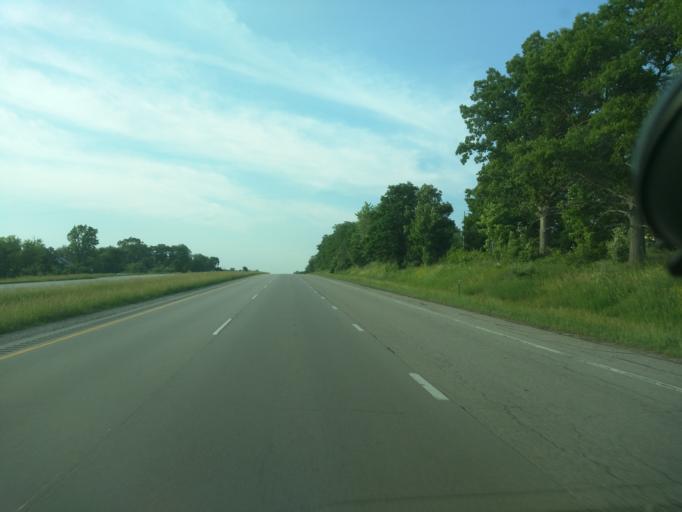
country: US
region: Michigan
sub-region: Ingham County
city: Leslie
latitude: 42.4541
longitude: -84.4435
